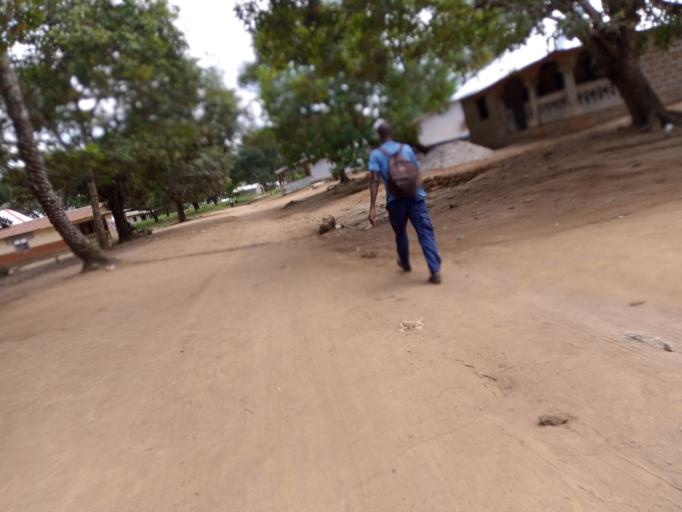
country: SL
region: Western Area
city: Waterloo
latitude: 8.3257
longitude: -13.0137
